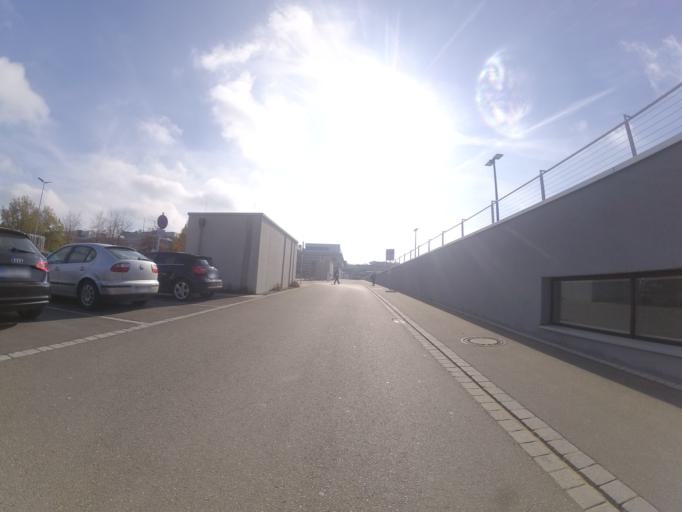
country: DE
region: Baden-Wuerttemberg
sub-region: Tuebingen Region
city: Dornstadt
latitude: 48.4237
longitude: 9.9516
